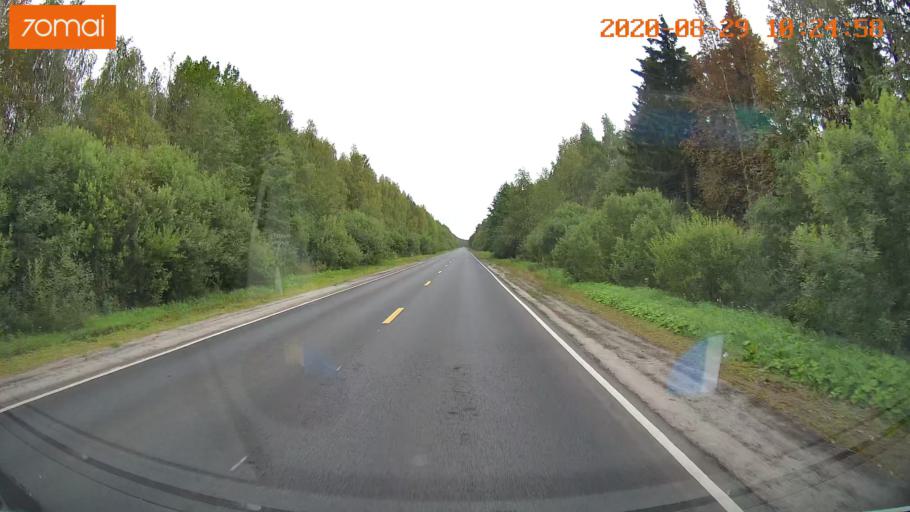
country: RU
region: Ivanovo
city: Yur'yevets
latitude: 57.3197
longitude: 43.0110
